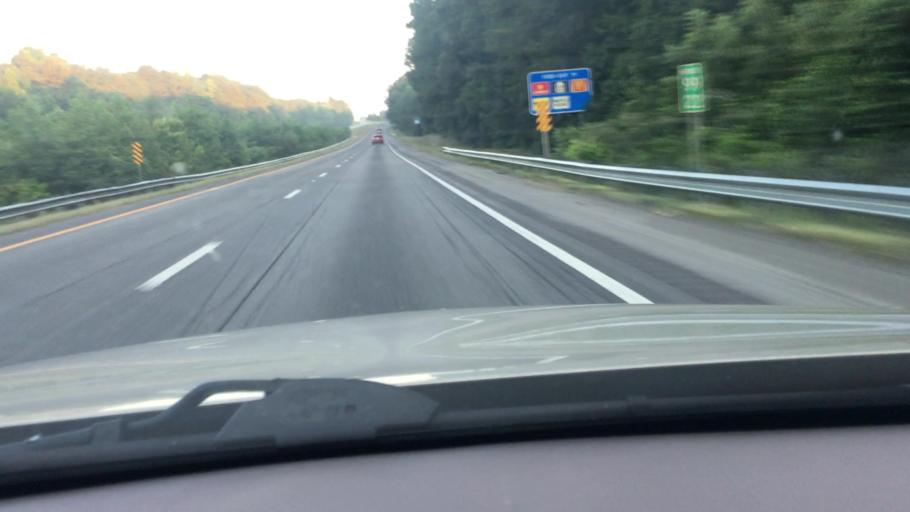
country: US
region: South Carolina
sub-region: Lexington County
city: Chapin
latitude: 34.1731
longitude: -81.3099
